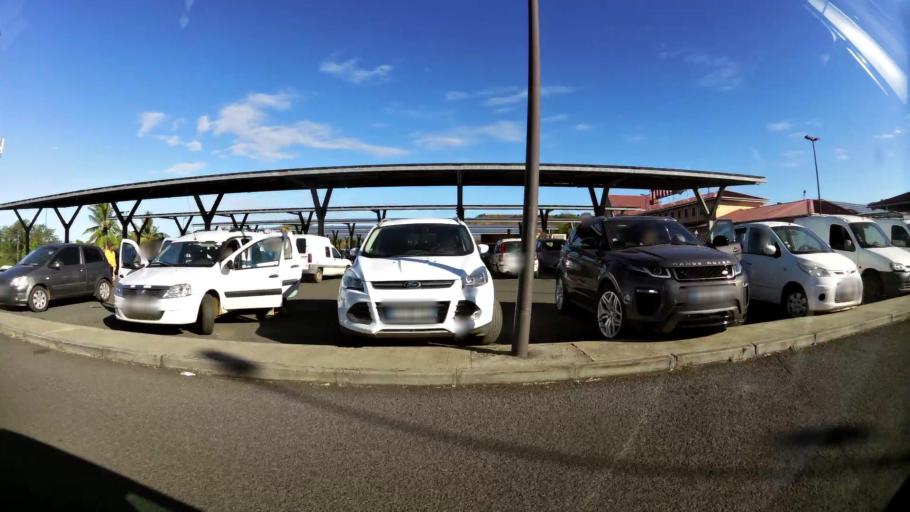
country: YT
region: Mamoudzou
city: Mamoudzou
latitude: -12.7561
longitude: 45.2324
